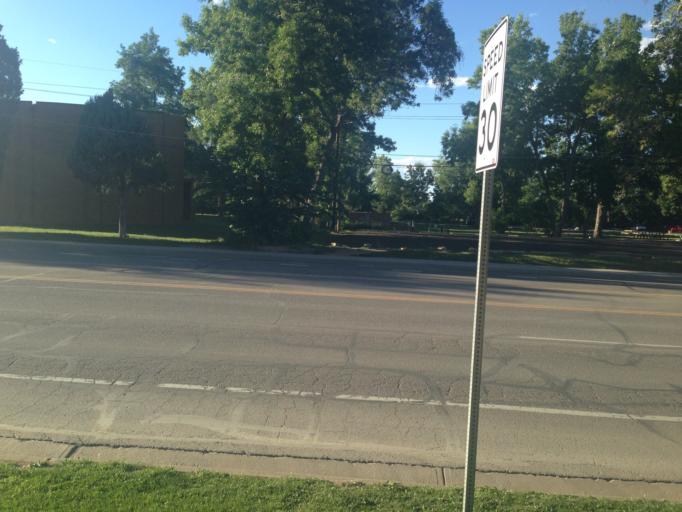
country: US
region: Colorado
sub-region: Boulder County
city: Boulder
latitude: 40.0082
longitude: -105.2634
